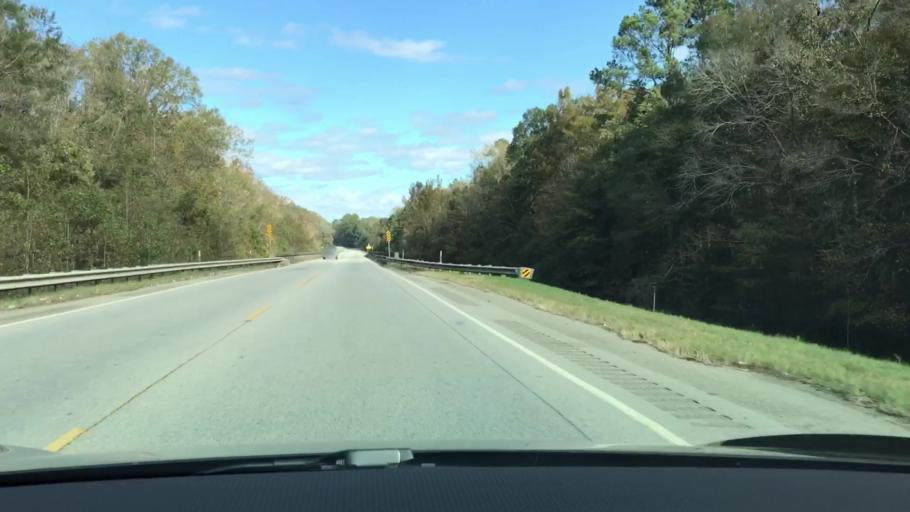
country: US
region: Georgia
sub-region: Jefferson County
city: Louisville
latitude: 32.9697
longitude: -82.3905
